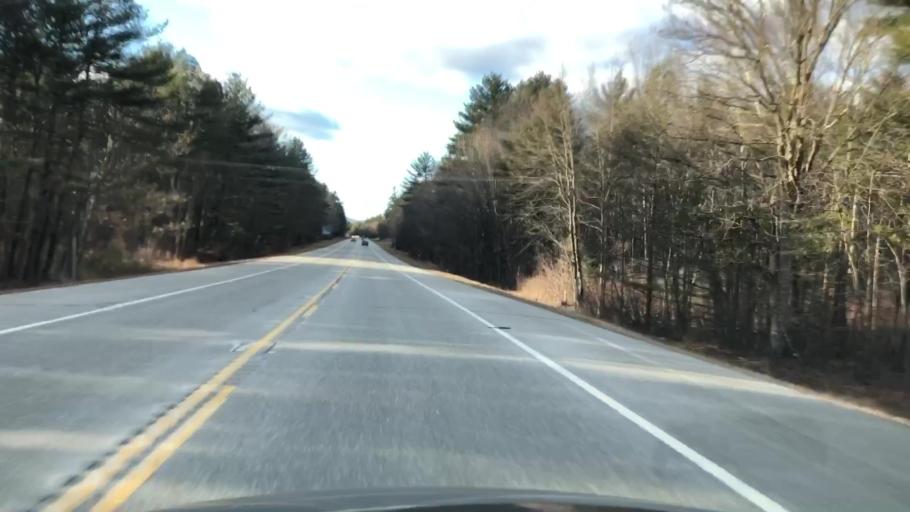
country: US
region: New Hampshire
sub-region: Hillsborough County
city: Milford
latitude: 42.8261
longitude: -71.6651
